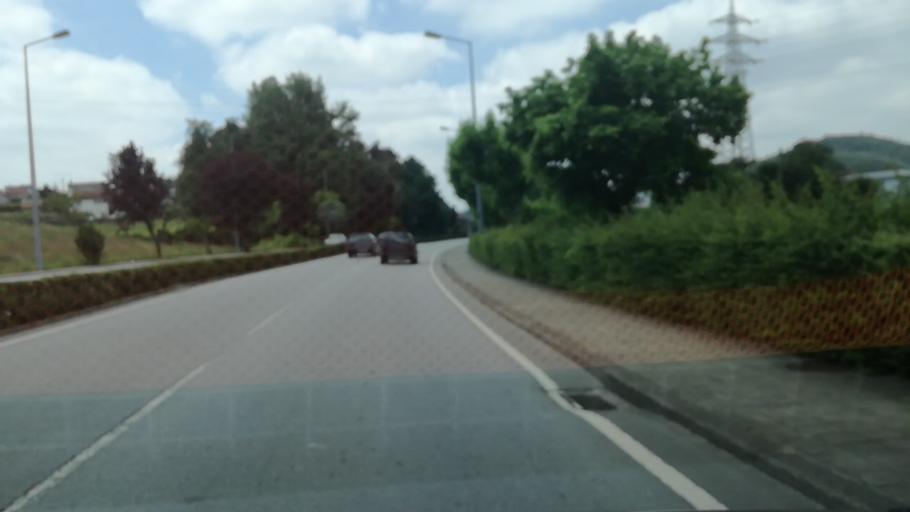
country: PT
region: Braga
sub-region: Vila Nova de Famalicao
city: Vila Nova de Famalicao
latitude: 41.3978
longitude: -8.5178
